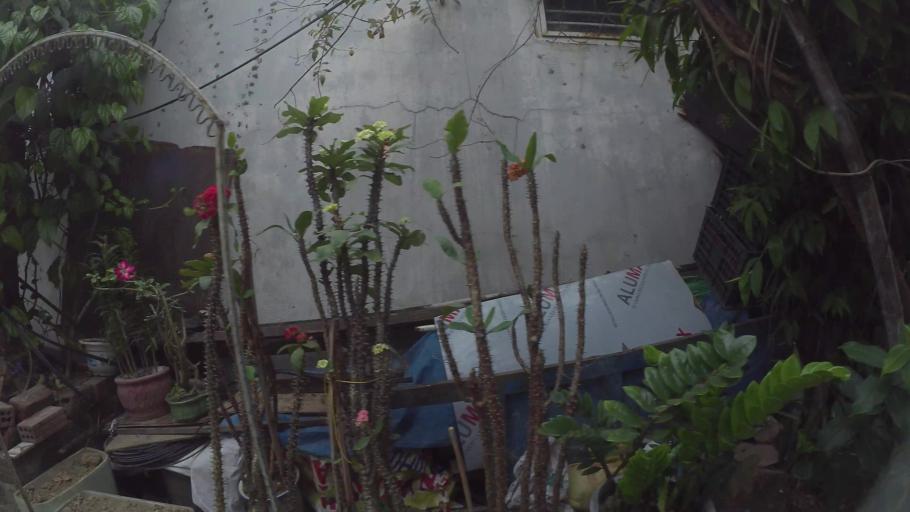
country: VN
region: Da Nang
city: Lien Chieu
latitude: 16.0728
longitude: 108.1519
